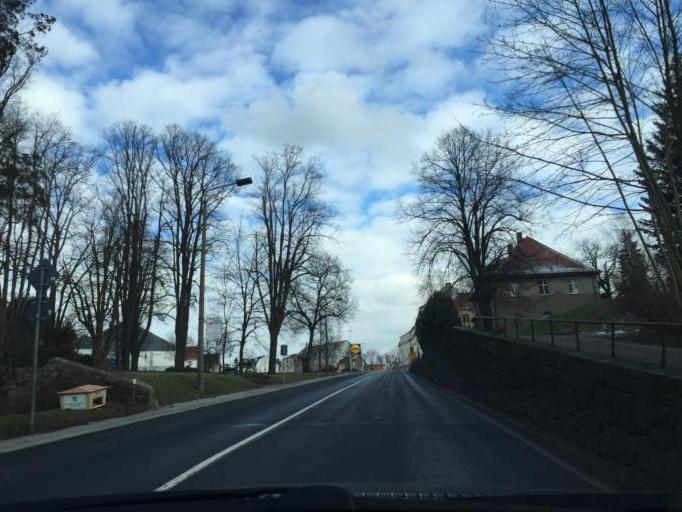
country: DE
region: Saxony
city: Radeberg
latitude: 51.1185
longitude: 13.9188
